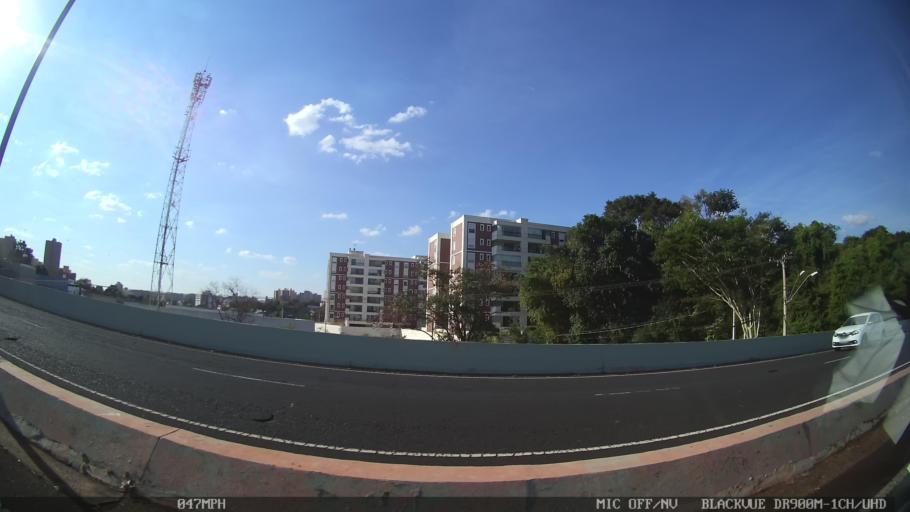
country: BR
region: Sao Paulo
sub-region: Ribeirao Preto
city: Ribeirao Preto
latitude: -21.1945
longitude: -47.7978
